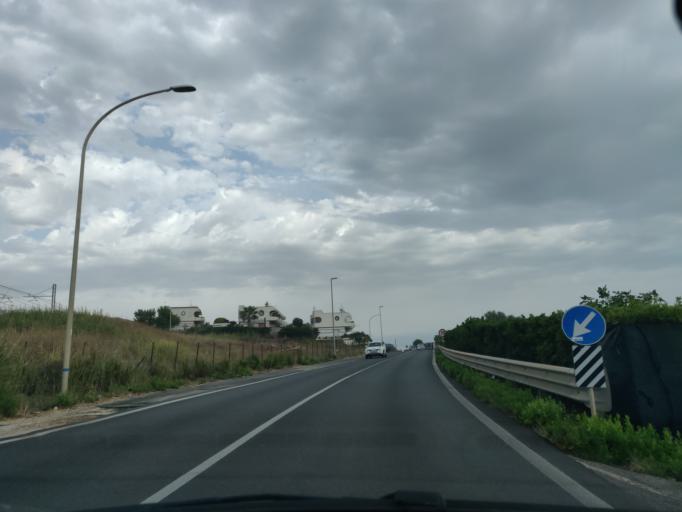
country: IT
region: Latium
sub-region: Citta metropolitana di Roma Capitale
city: Santa Marinella
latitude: 42.0399
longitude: 11.8964
